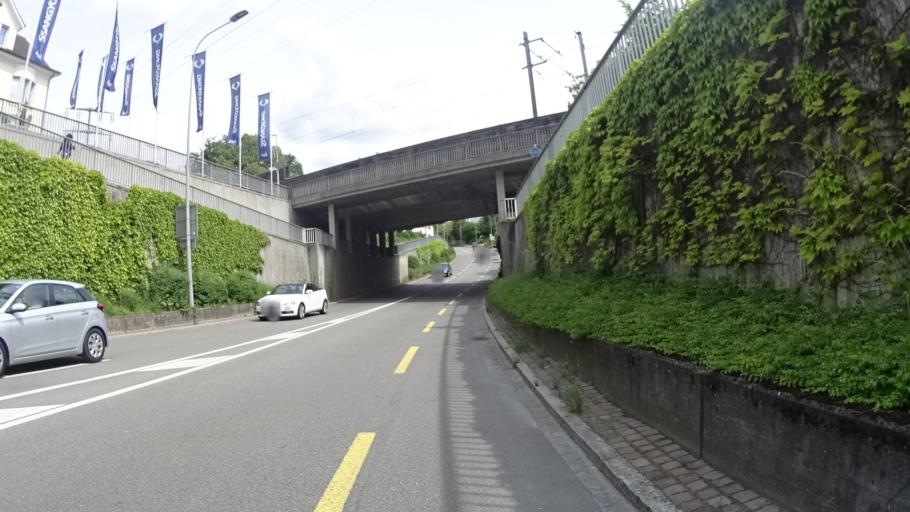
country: CH
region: Aargau
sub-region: Bezirk Rheinfelden
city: Rheinfelden
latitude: 47.5528
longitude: 7.7963
